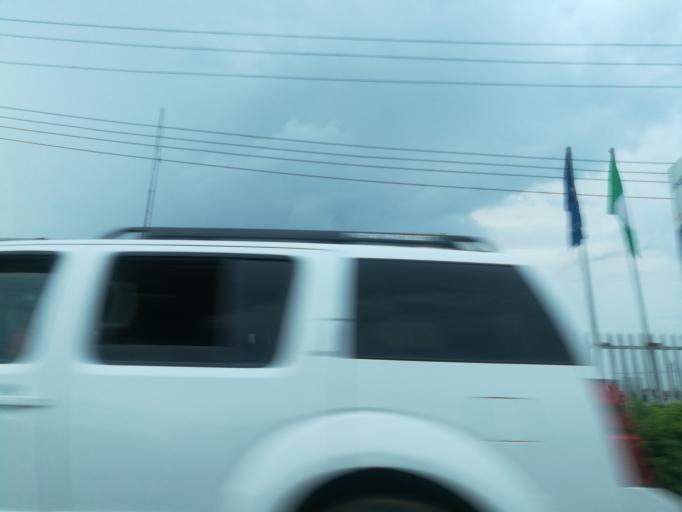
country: NG
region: Oyo
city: Moniya
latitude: 7.4622
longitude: 3.9120
